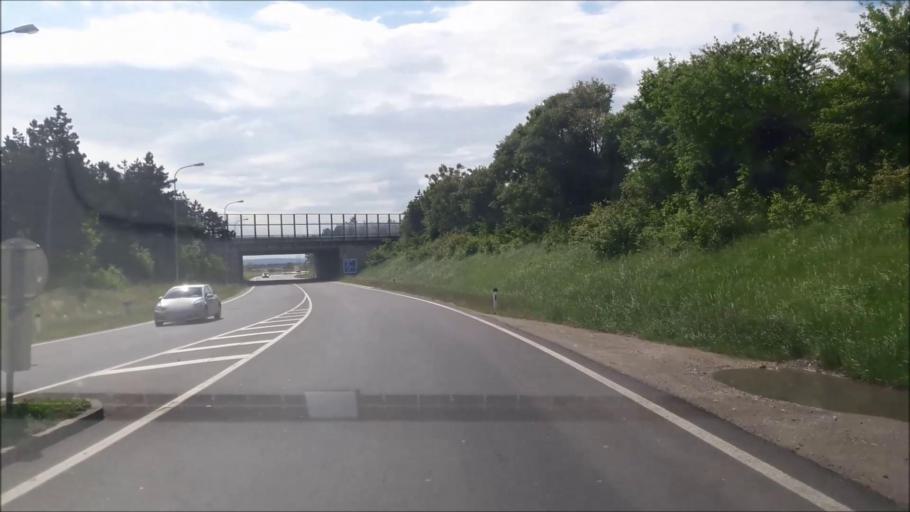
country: AT
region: Lower Austria
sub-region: Politischer Bezirk Wiener Neustadt
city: Theresienfeld
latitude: 47.8583
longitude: 16.1834
